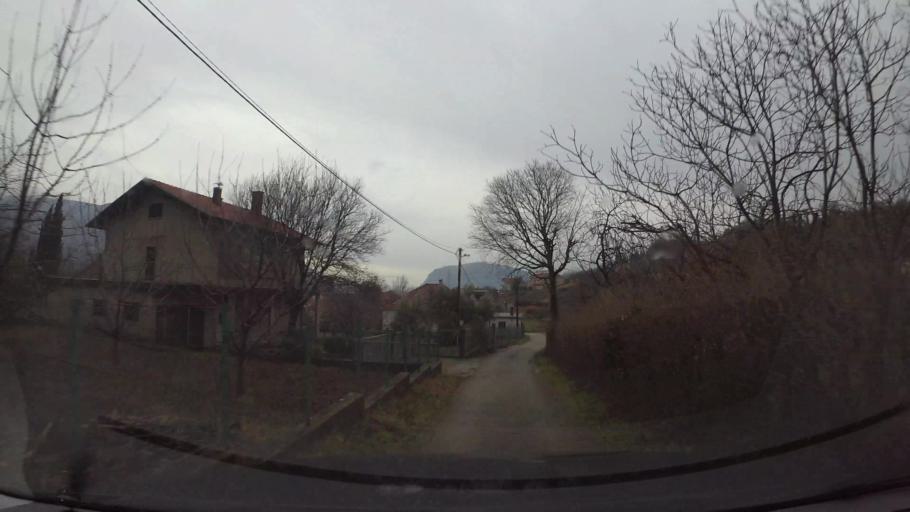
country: BA
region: Federation of Bosnia and Herzegovina
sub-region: Hercegovacko-Bosanski Kanton
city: Mostar
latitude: 43.3694
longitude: 17.8075
